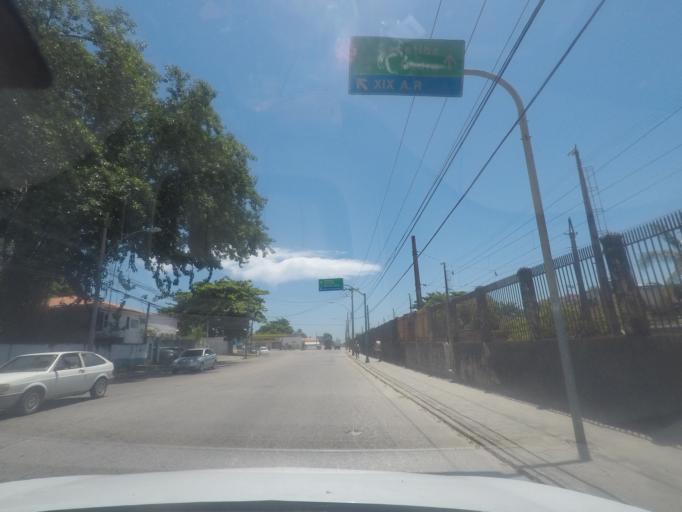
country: BR
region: Rio de Janeiro
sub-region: Itaguai
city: Itaguai
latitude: -22.9191
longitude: -43.6884
